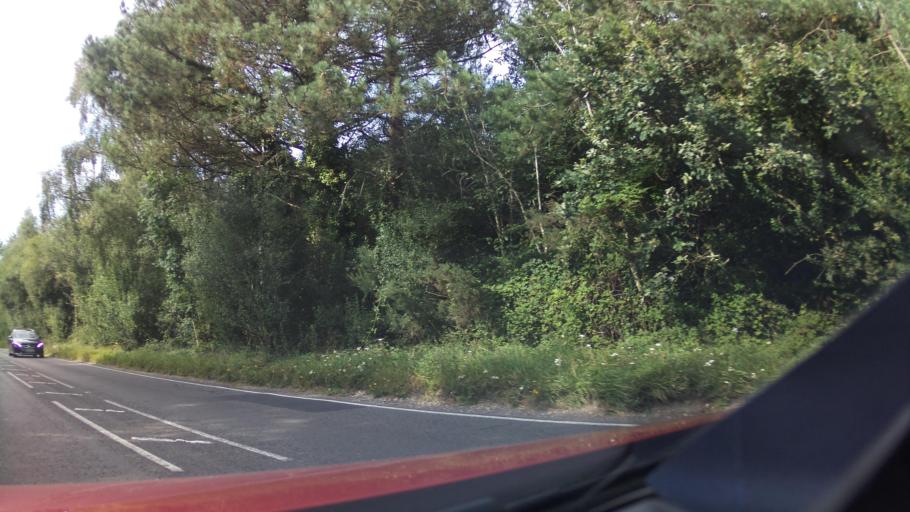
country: GB
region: England
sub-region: Hampshire
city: Hythe
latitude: 50.8554
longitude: -1.4251
